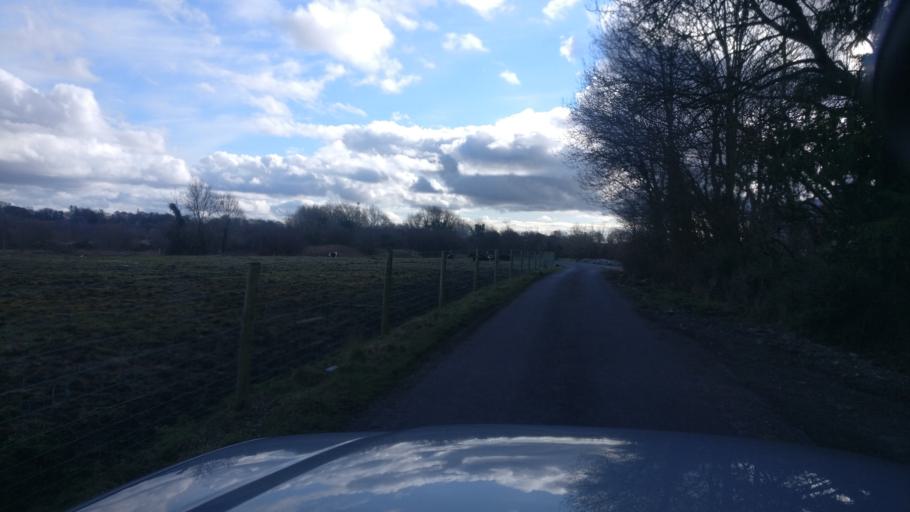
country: IE
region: Connaught
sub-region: County Galway
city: Loughrea
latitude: 53.1924
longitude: -8.4299
